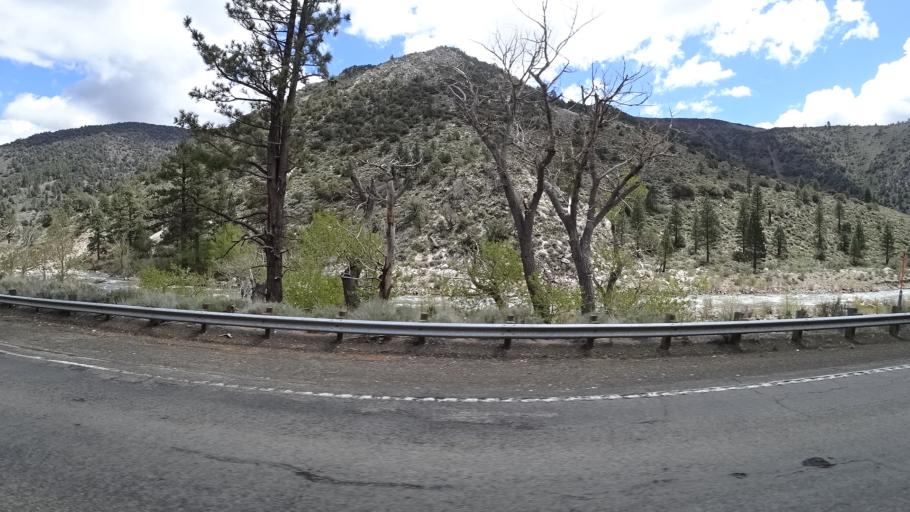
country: US
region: California
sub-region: Mono County
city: Bridgeport
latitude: 38.4146
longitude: -119.4507
